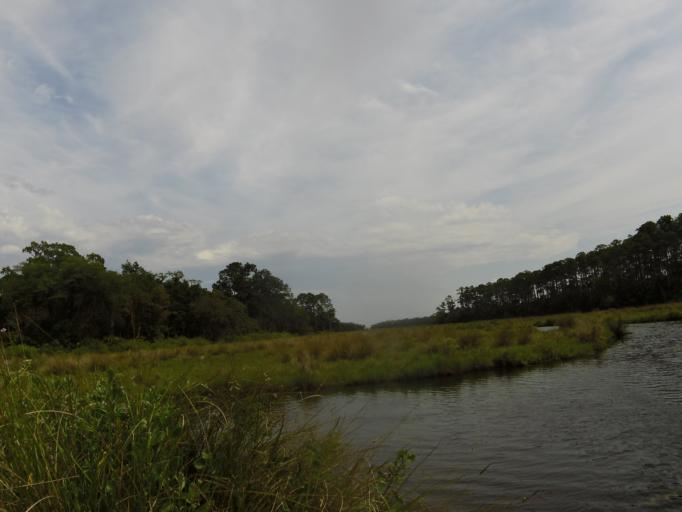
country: US
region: Florida
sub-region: Volusia County
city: Ormond-by-the-Sea
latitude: 29.3996
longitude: -81.1225
